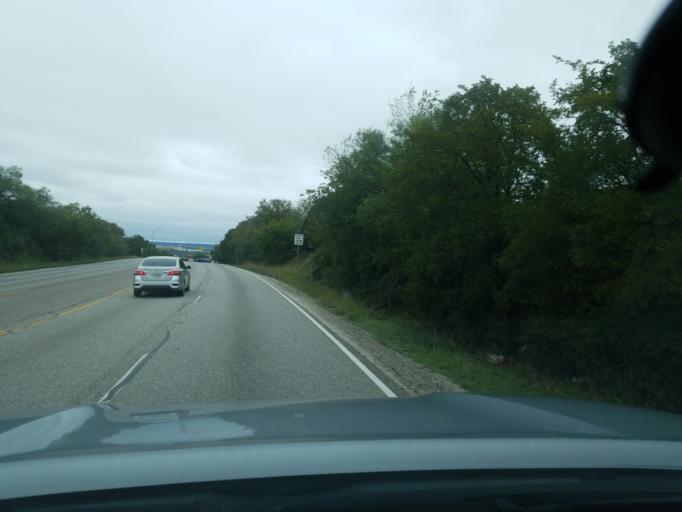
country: US
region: Texas
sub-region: Burnet County
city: Marble Falls
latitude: 30.5576
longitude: -98.2744
